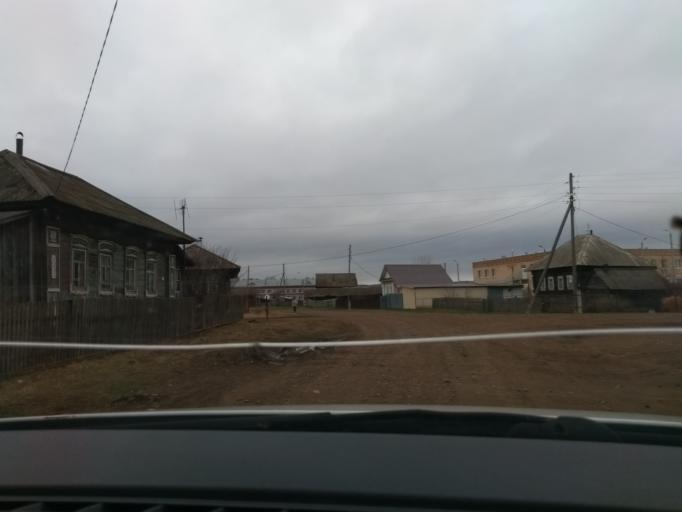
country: RU
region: Perm
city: Orda
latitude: 57.2146
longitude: 56.5954
